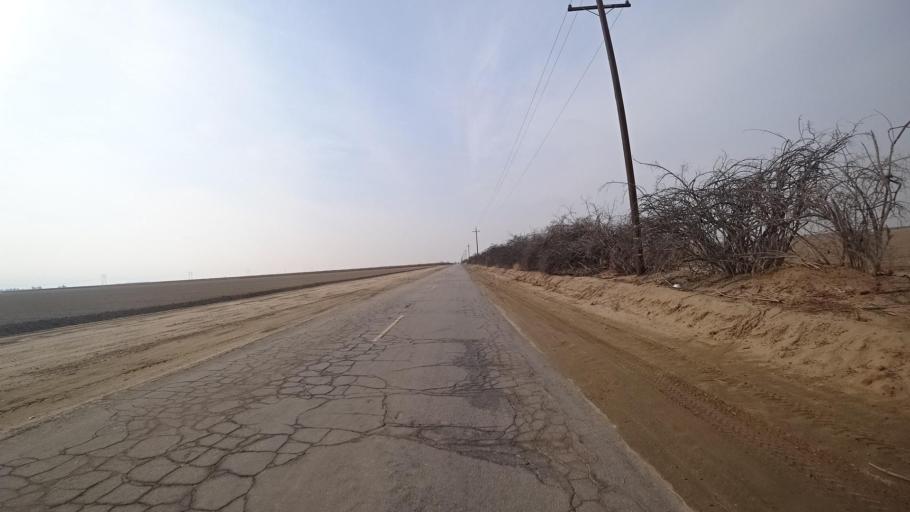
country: US
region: California
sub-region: Kern County
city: Weedpatch
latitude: 35.1365
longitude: -118.9201
